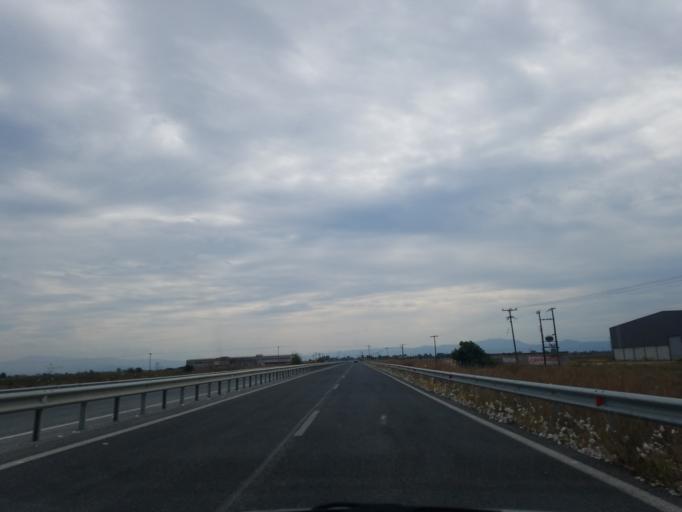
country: GR
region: Thessaly
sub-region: Nomos Kardhitsas
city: Sofades
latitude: 39.3128
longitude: 22.1184
